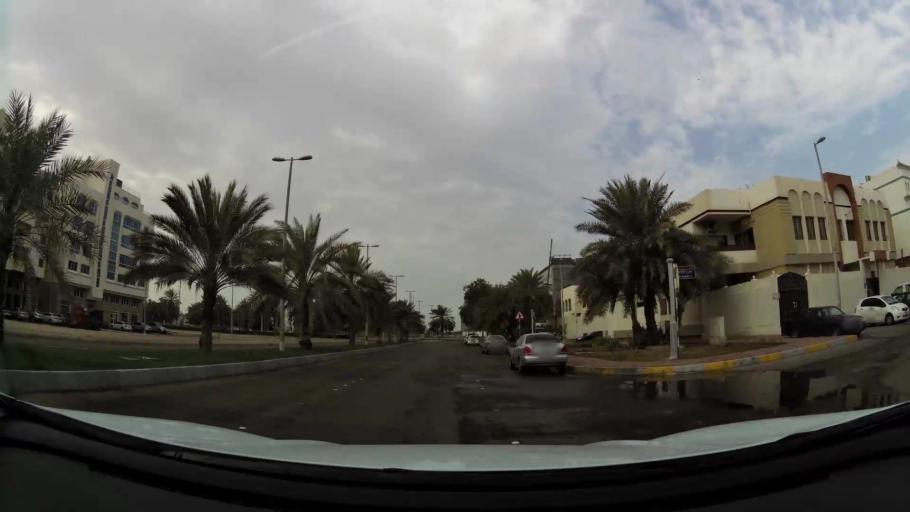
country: AE
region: Abu Dhabi
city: Abu Dhabi
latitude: 24.4502
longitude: 54.3996
